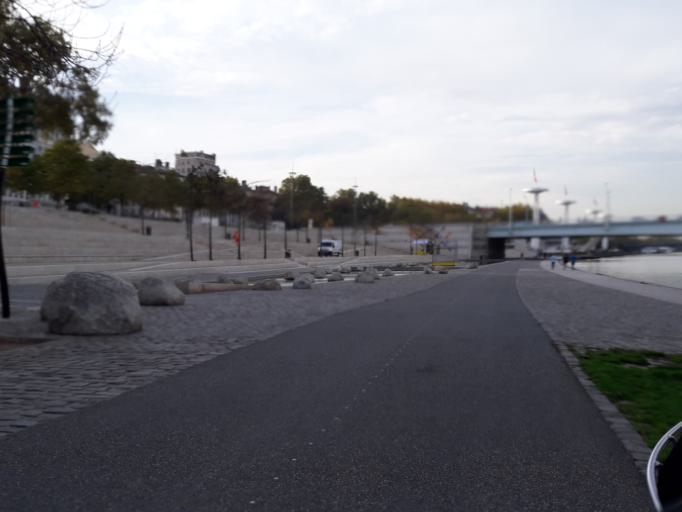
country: FR
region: Rhone-Alpes
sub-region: Departement du Rhone
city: Lyon
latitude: 45.7582
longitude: 4.8402
